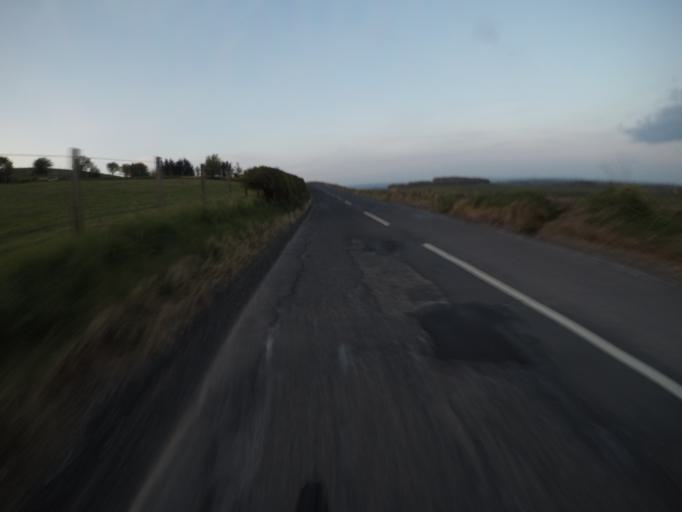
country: GB
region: Scotland
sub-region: South Ayrshire
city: Dundonald
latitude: 55.5638
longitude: -4.6040
